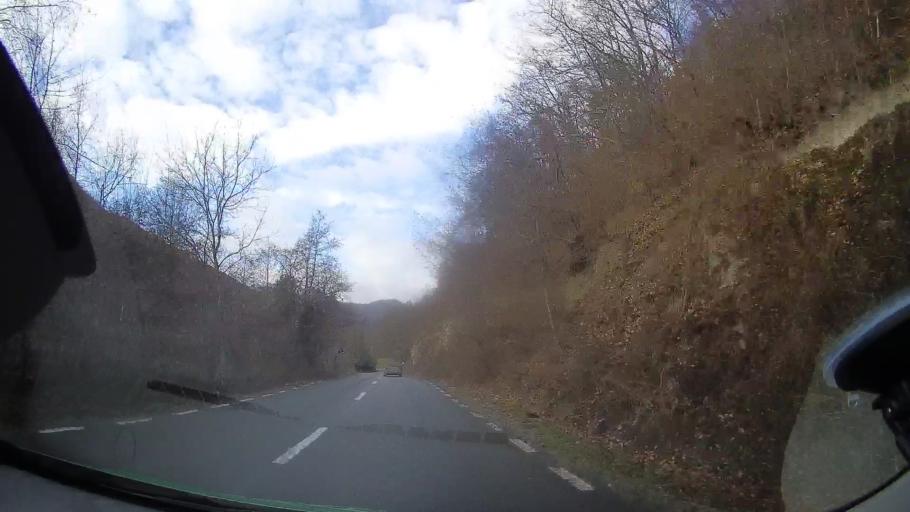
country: RO
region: Cluj
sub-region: Comuna Baisoara
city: Baisoara
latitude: 46.6095
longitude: 23.4170
